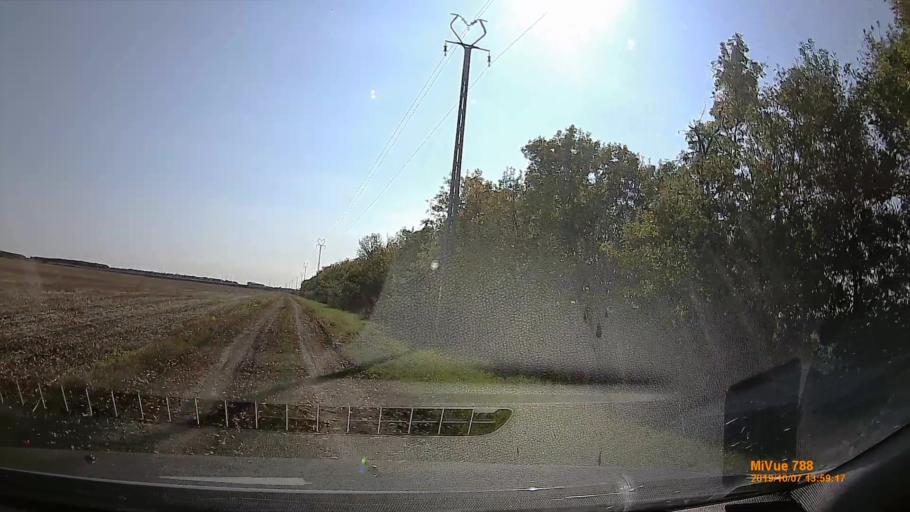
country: HU
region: Jasz-Nagykun-Szolnok
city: Cserkeszolo
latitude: 46.8909
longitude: 20.2145
